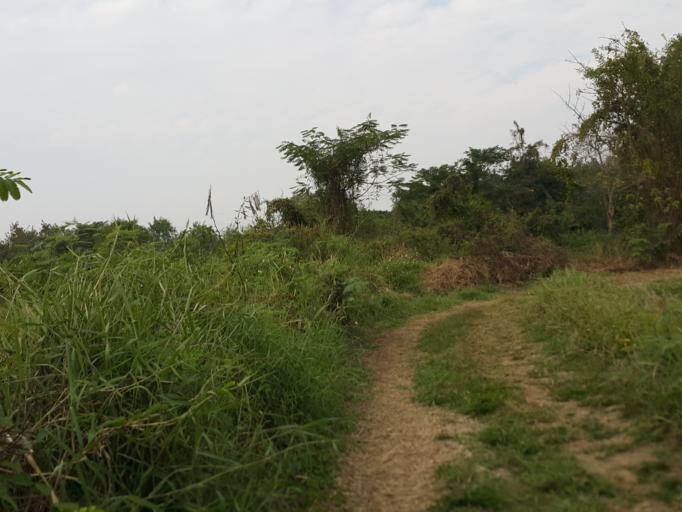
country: TH
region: Chiang Mai
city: San Kamphaeng
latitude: 18.8011
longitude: 99.1157
